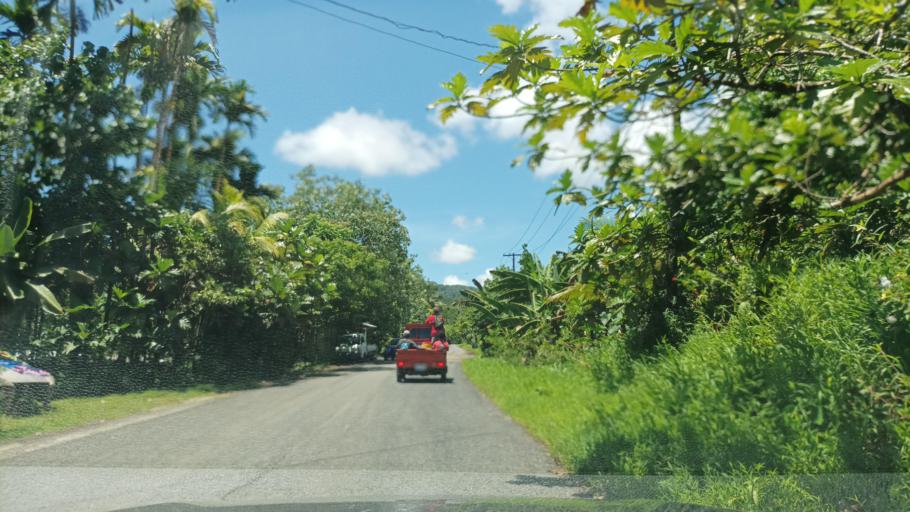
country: FM
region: Pohnpei
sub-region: Kolonia Municipality
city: Kolonia
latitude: 6.9317
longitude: 158.2778
